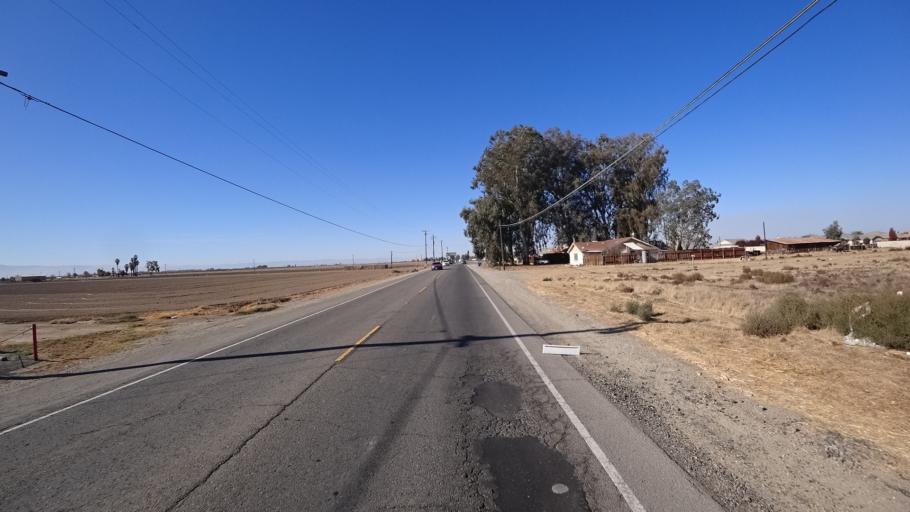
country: US
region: California
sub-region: Kern County
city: Greenfield
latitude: 35.2669
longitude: -119.0441
